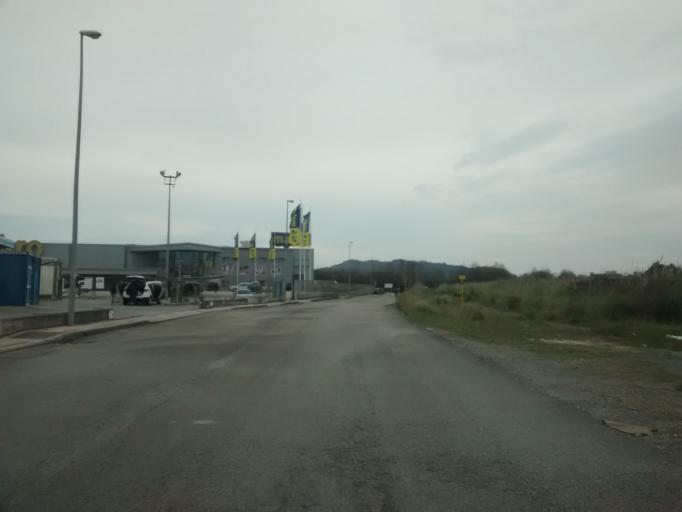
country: ES
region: Cantabria
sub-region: Provincia de Cantabria
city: El Astillero
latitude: 43.4257
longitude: -3.8406
